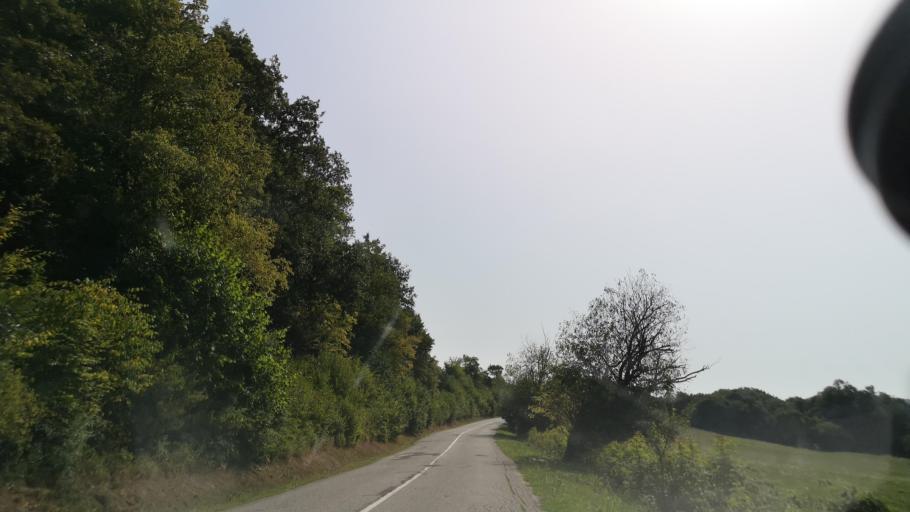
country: SK
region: Banskobystricky
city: Revuca
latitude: 48.6143
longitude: 20.2166
